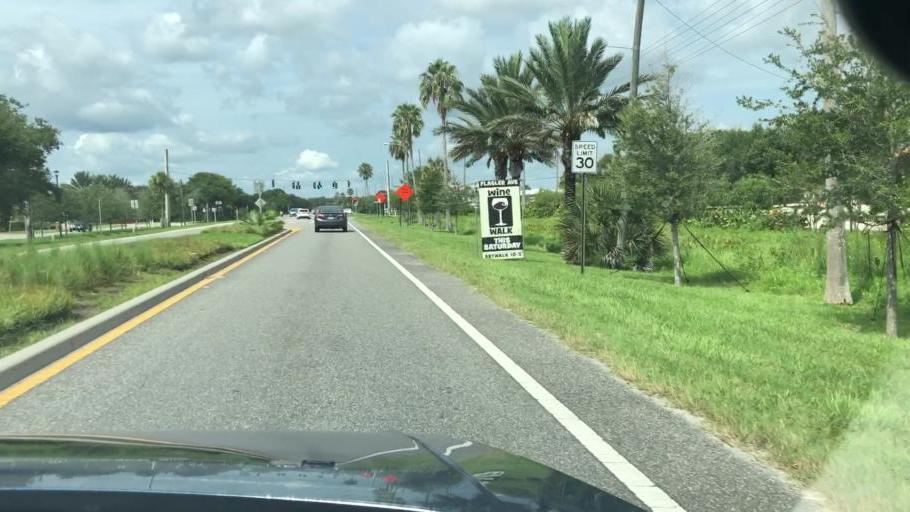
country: US
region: Florida
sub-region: Volusia County
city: New Smyrna Beach
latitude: 29.0345
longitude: -80.9139
